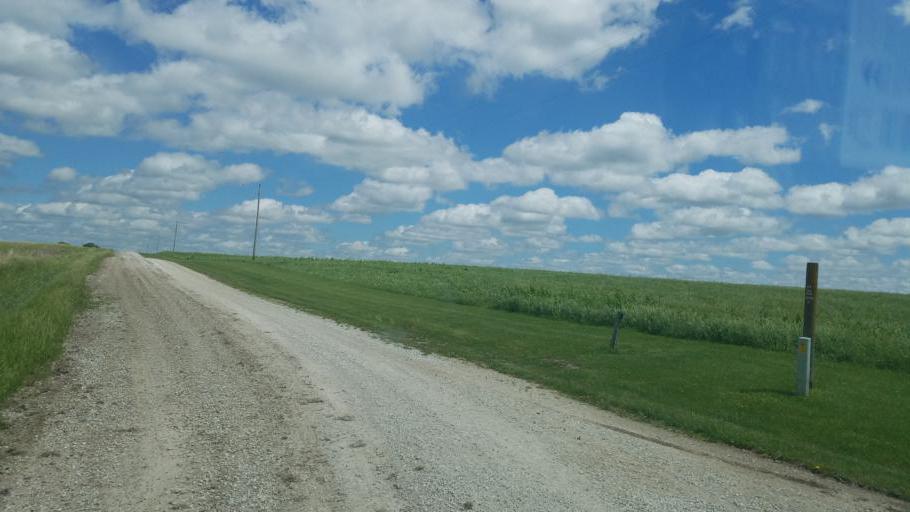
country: US
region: Iowa
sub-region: Decatur County
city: Lamoni
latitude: 40.4969
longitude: -93.9837
